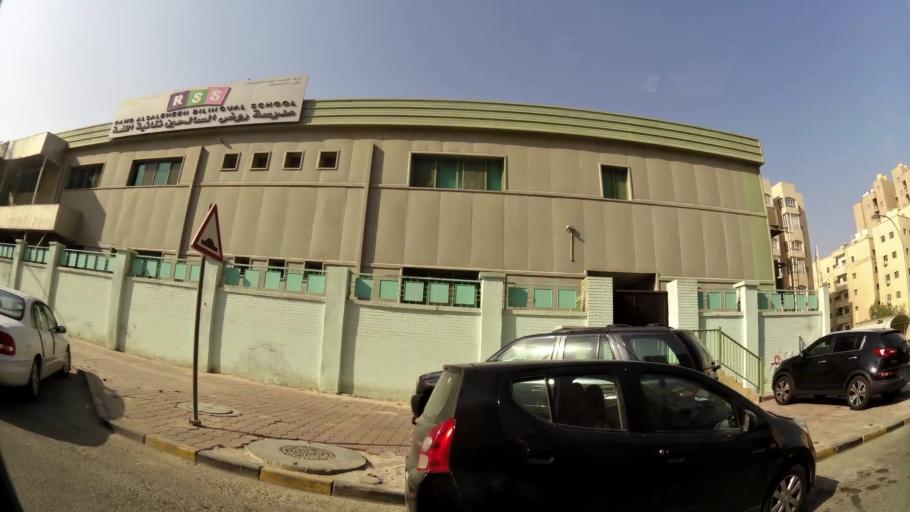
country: KW
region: Muhafazat Hawalli
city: Hawalli
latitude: 29.3364
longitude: 48.0069
